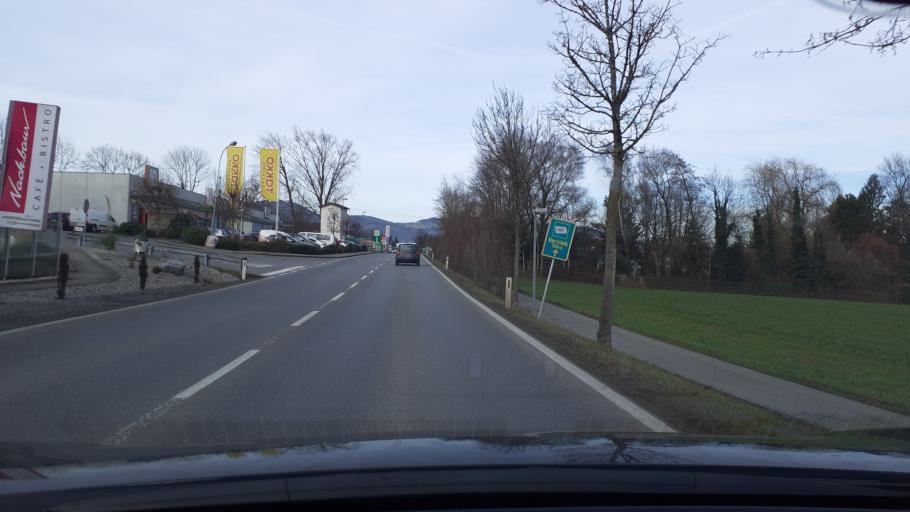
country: AT
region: Vorarlberg
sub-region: Politischer Bezirk Dornbirn
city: Hohenems
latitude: 47.3726
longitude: 9.6805
